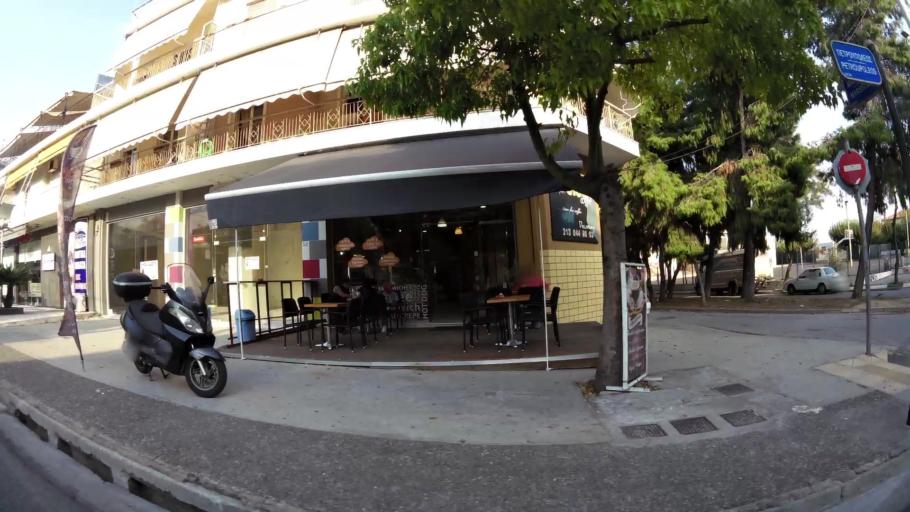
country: GR
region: Attica
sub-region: Nomarchia Athinas
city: Ilion
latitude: 38.0331
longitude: 23.6962
